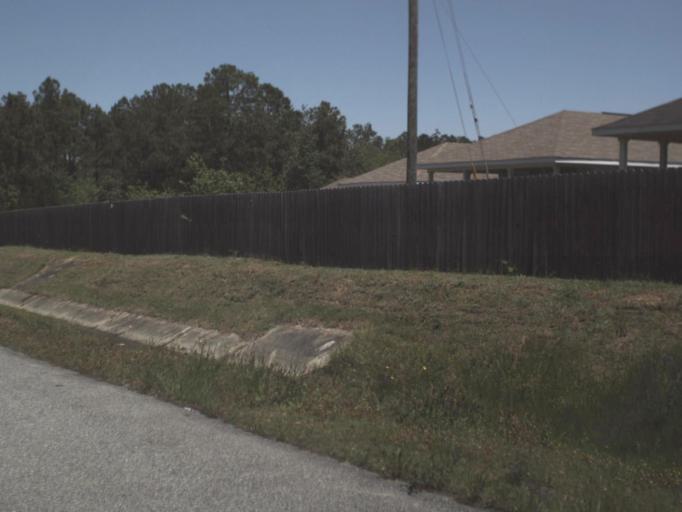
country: US
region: Florida
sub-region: Escambia County
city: Bellview
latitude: 30.4836
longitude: -87.3234
